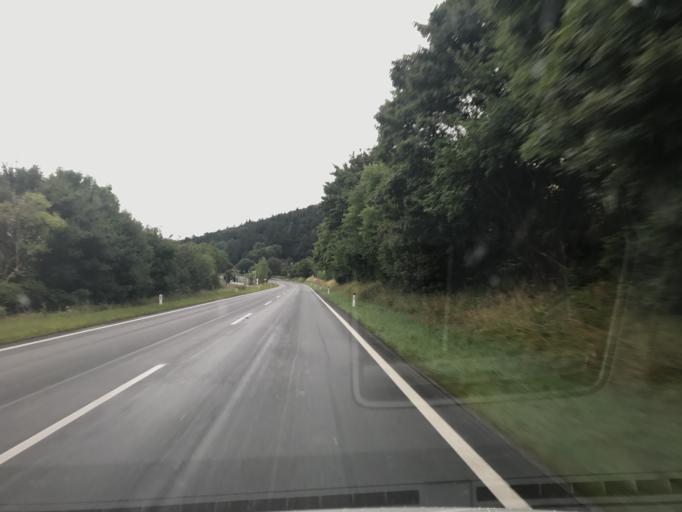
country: AT
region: Lower Austria
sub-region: Politischer Bezirk Wiener Neustadt
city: Markt Piesting
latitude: 47.8663
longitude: 16.1620
